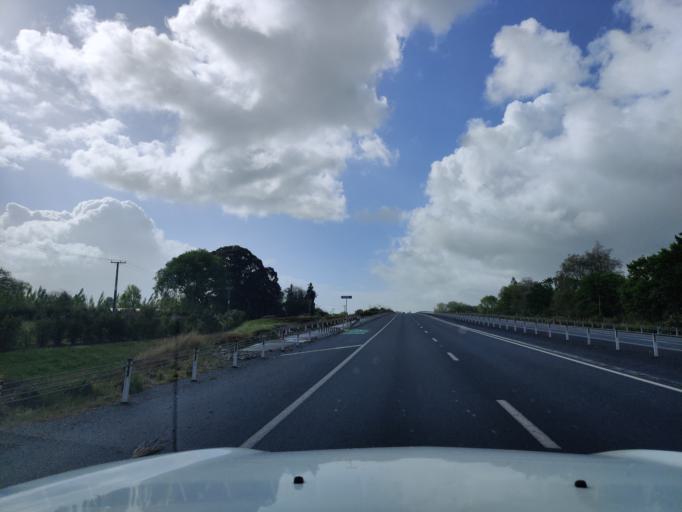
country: NZ
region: Waikato
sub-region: Waipa District
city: Cambridge
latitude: -37.8435
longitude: 175.3749
